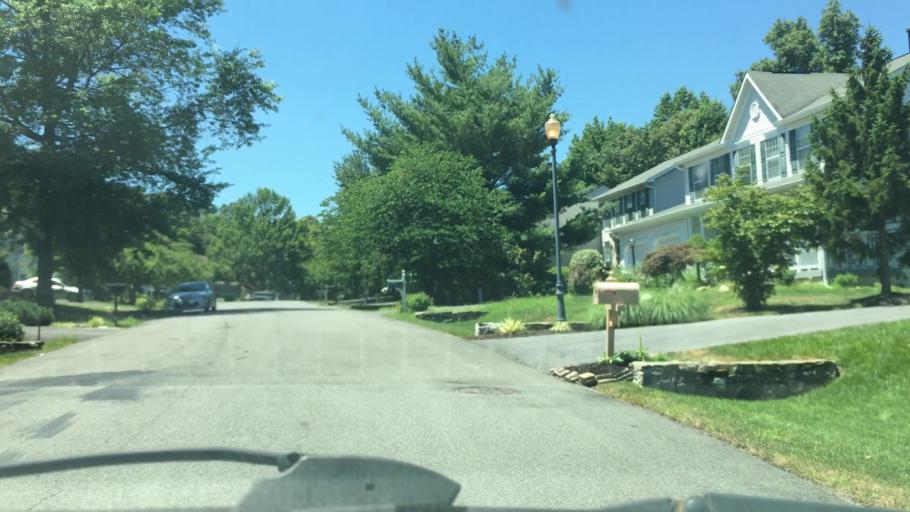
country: US
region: Maryland
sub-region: Prince George's County
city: Glenn Dale
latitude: 38.9953
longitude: -76.7838
